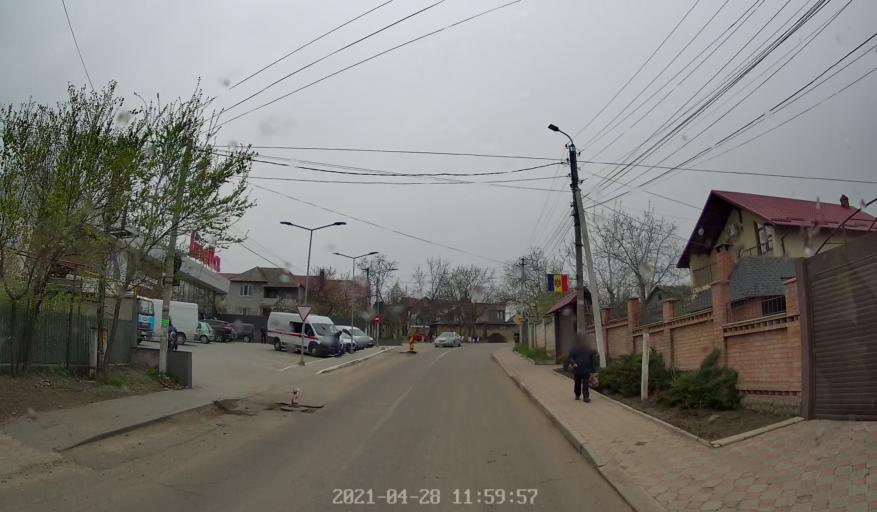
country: MD
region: Chisinau
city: Singera
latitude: 46.9839
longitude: 28.9323
